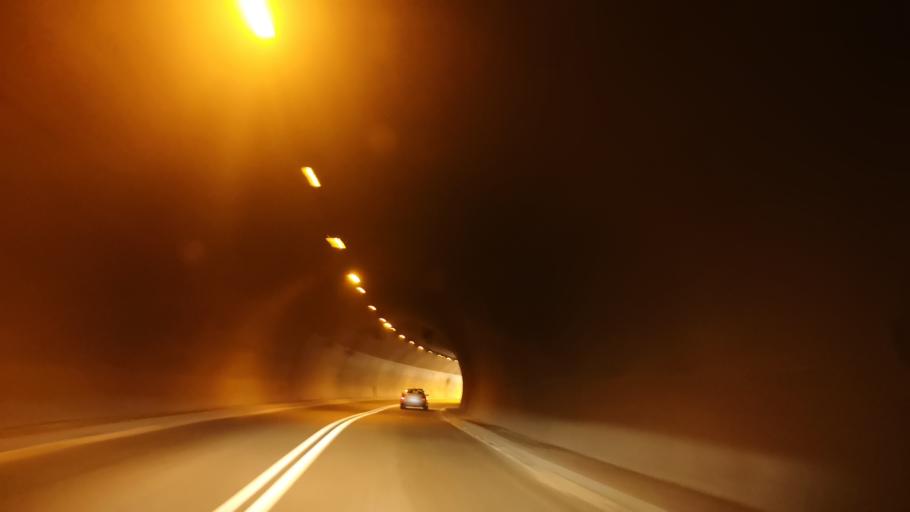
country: RS
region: Central Serbia
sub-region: Moravicki Okrug
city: Lucani
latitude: 43.9005
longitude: 20.1834
